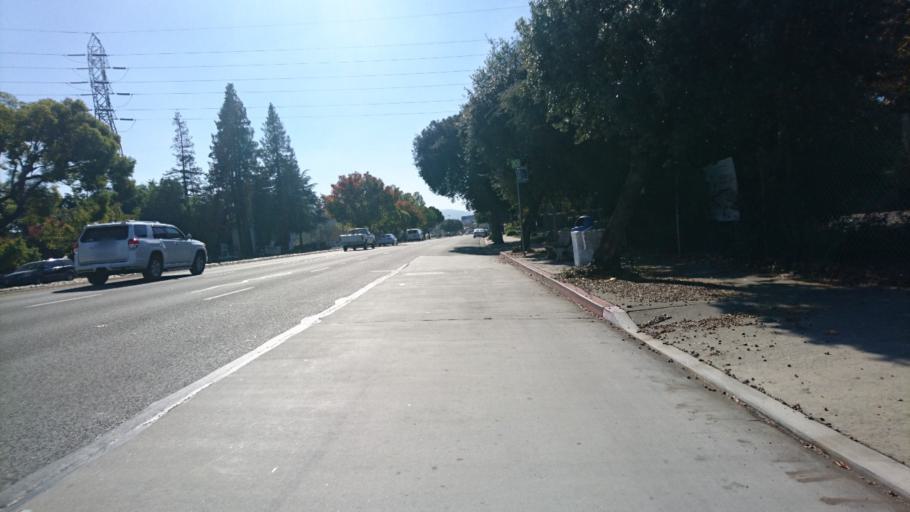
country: US
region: California
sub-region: Santa Clara County
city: Campbell
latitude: 37.2772
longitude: -121.9325
